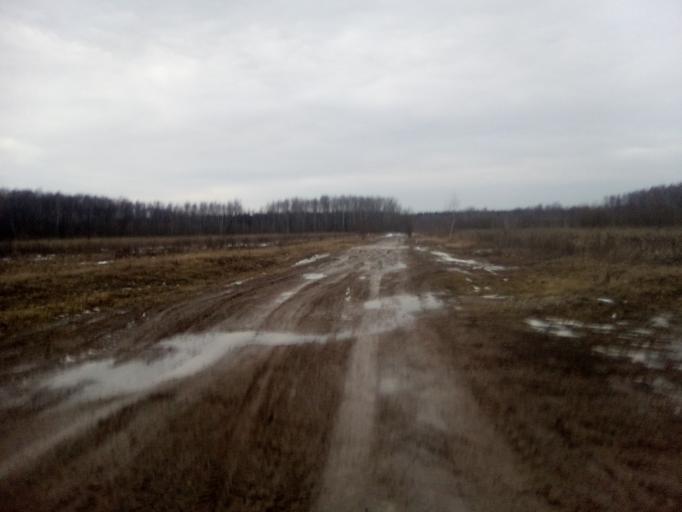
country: RU
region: Moskovskaya
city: Filimonki
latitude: 55.5107
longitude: 37.4141
